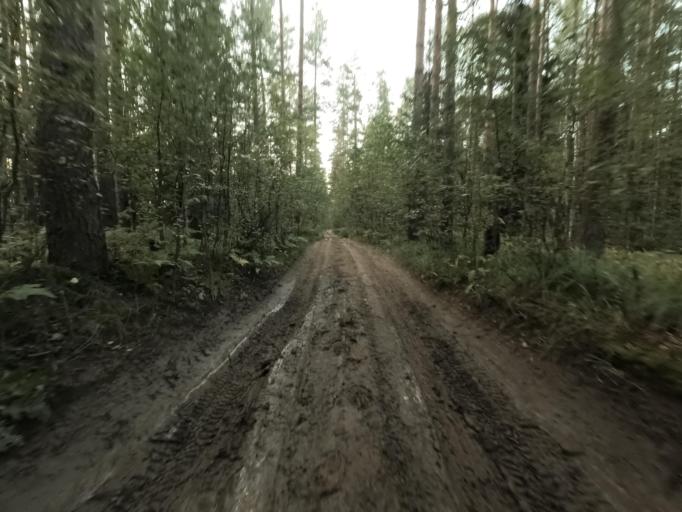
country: RU
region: Leningrad
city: Otradnoye
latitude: 59.8440
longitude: 30.8013
